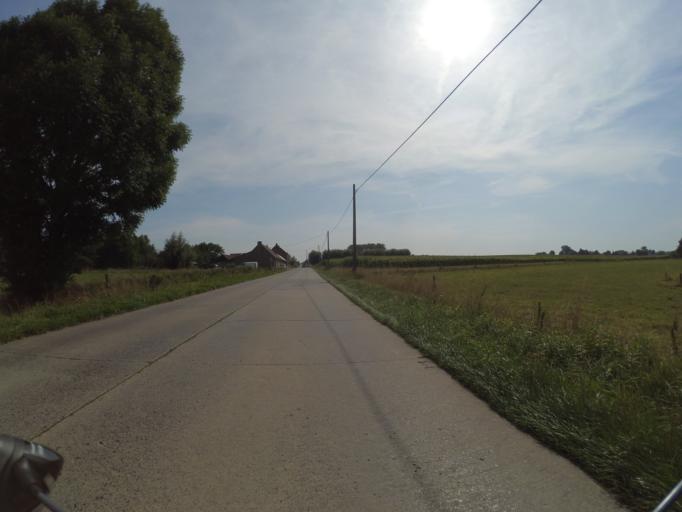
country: BE
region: Wallonia
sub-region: Province du Hainaut
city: Flobecq
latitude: 50.7269
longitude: 3.7205
